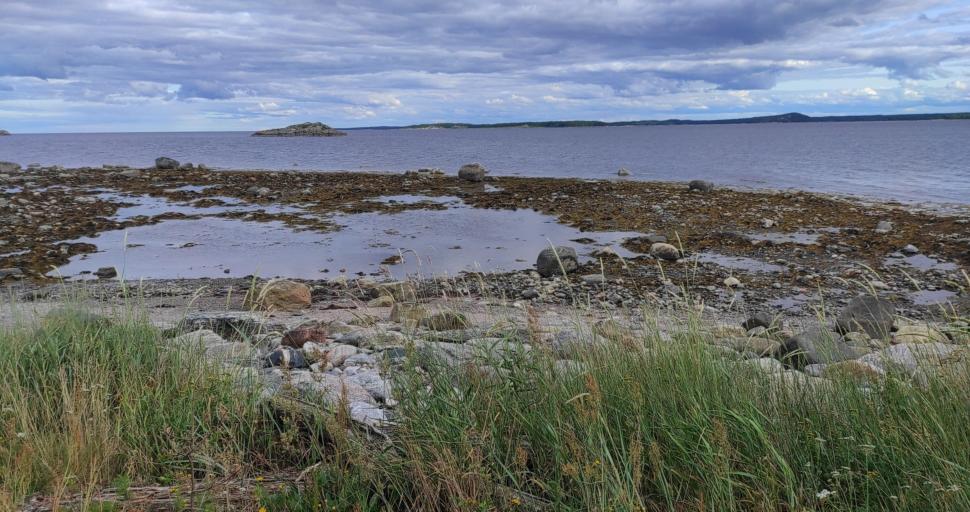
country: RU
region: Murmansk
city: Poyakonda
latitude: 66.7256
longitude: 32.9483
